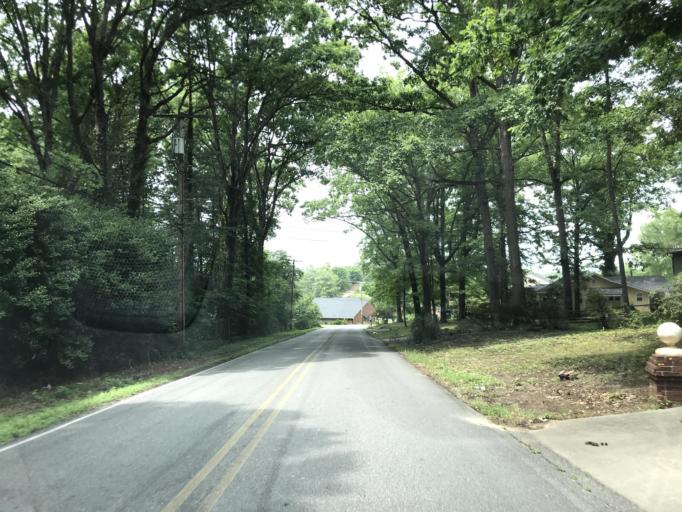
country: US
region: North Carolina
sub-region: Lincoln County
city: Lincolnton
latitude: 35.4816
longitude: -81.2518
